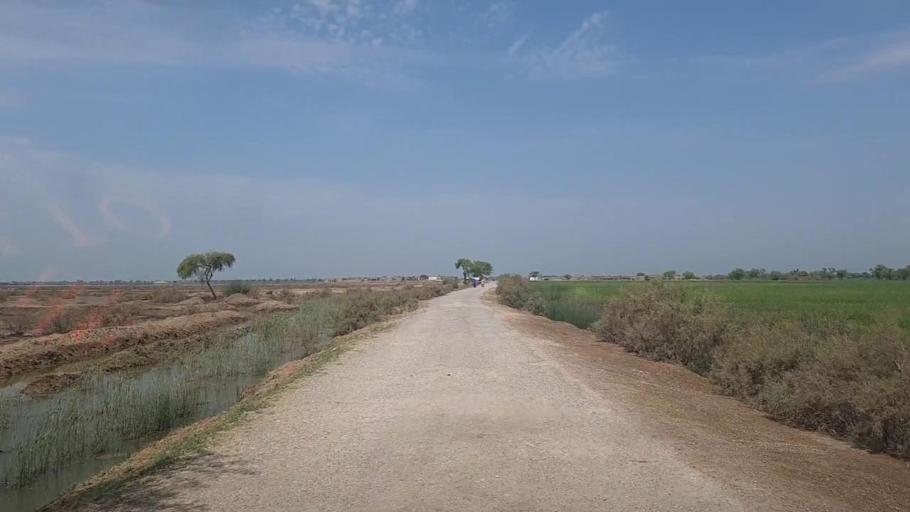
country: PK
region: Sindh
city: Thul
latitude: 28.2875
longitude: 68.6847
